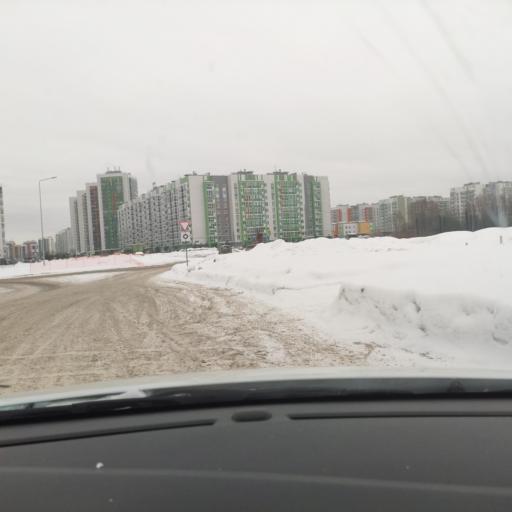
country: RU
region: Tatarstan
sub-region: Gorod Kazan'
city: Kazan
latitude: 55.7886
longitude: 49.2513
